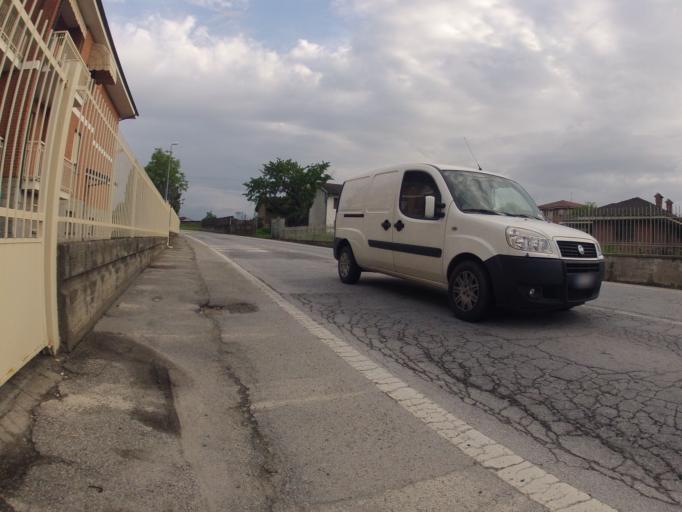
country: IT
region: Piedmont
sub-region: Provincia di Cuneo
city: Moretta
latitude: 44.7631
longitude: 7.5318
